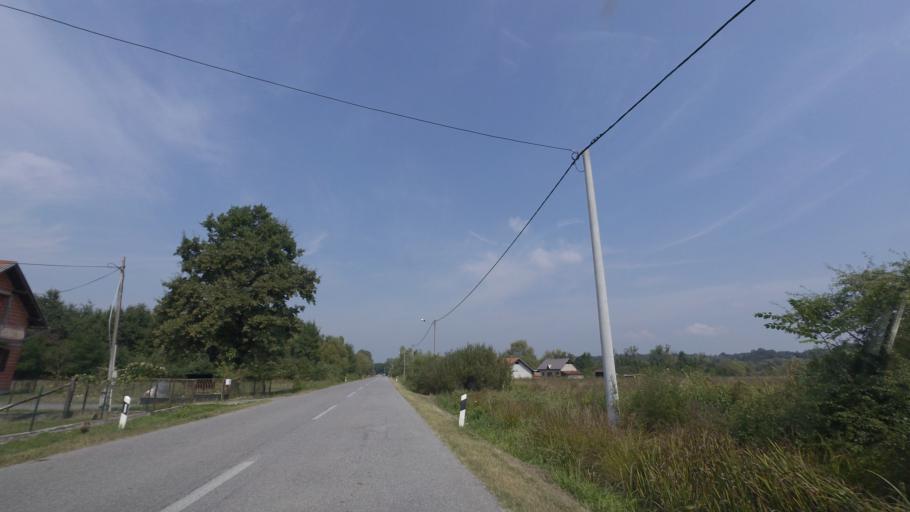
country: HR
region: Sisacko-Moslavacka
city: Glina
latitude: 45.2912
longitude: 16.1374
